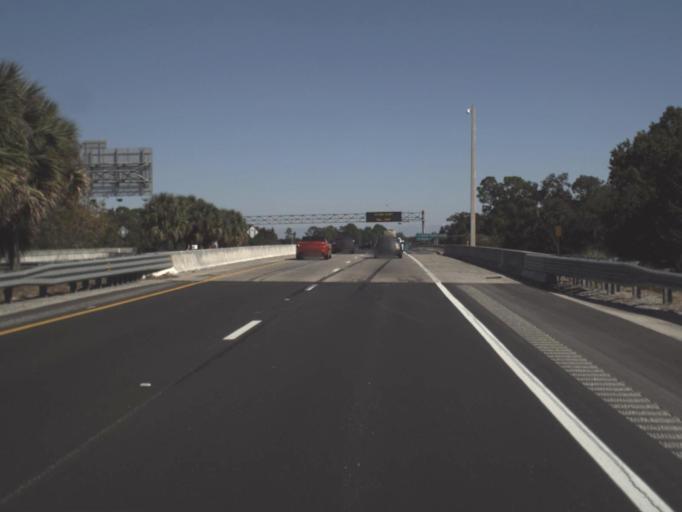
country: US
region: Florida
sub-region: Seminole County
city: Lake Mary
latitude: 28.7994
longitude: -81.3171
